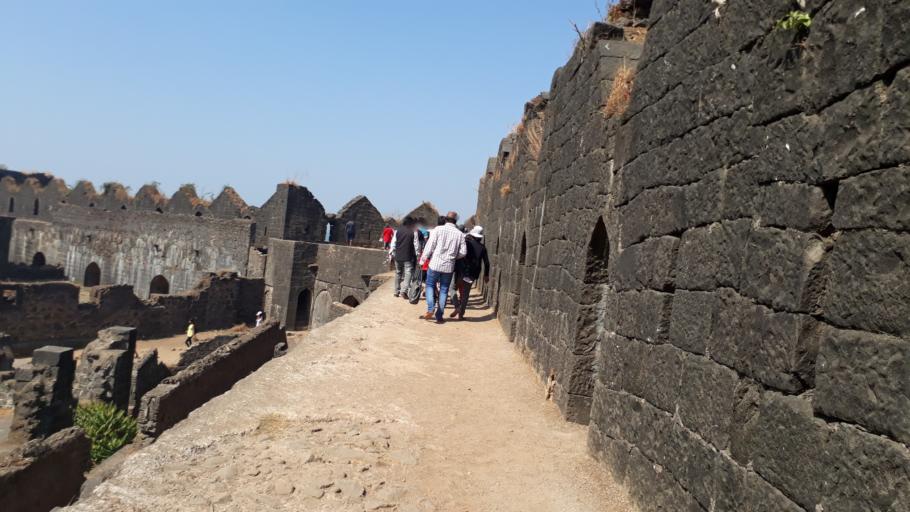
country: IN
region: Maharashtra
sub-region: Raigarh
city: Murud
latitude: 18.3007
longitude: 72.9653
